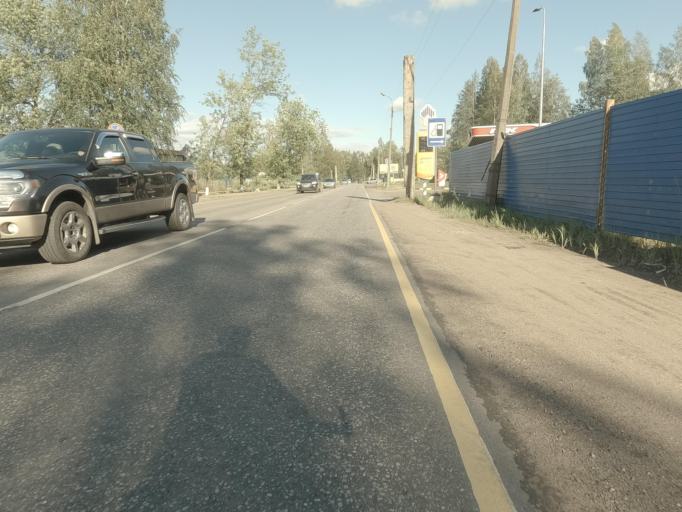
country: RU
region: Leningrad
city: Imeni Morozova
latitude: 59.9734
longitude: 31.0156
